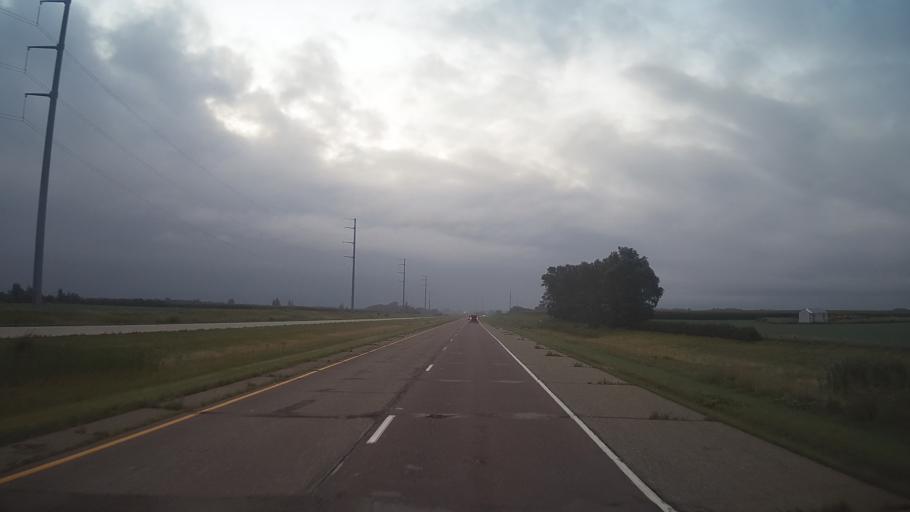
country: US
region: Minnesota
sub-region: Jackson County
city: Lakefield
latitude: 43.6374
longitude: -95.3485
